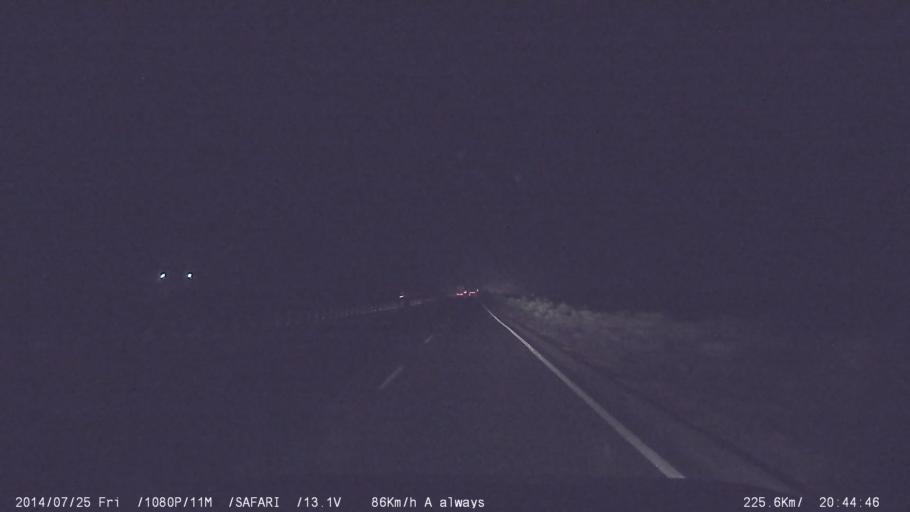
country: IN
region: Tamil Nadu
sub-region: Salem
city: Konganapuram
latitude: 11.5107
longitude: 77.9205
